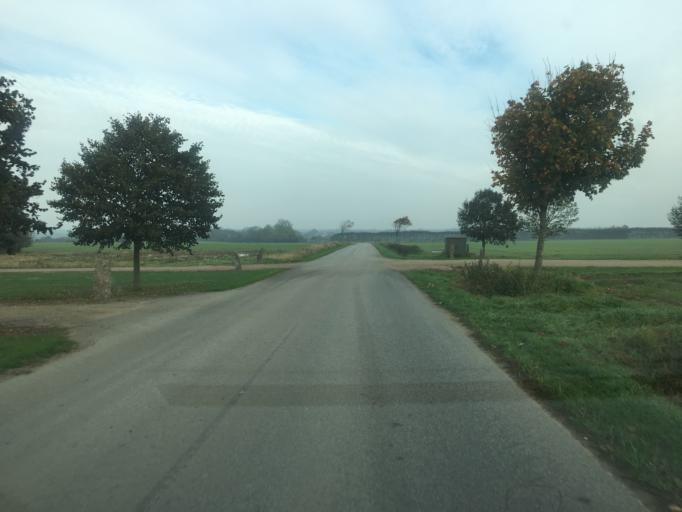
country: DK
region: South Denmark
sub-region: Tonder Kommune
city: Toftlund
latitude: 55.1056
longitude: 9.0888
